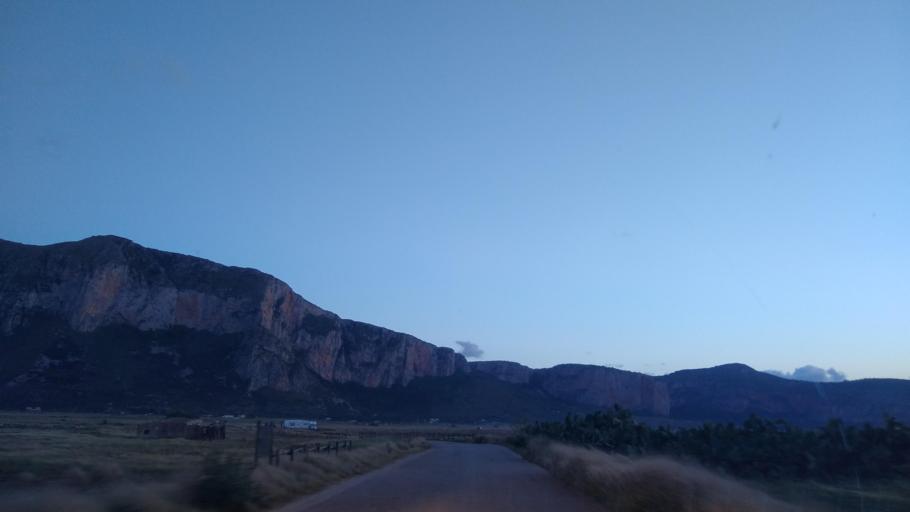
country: IT
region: Sicily
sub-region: Trapani
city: Castelluzzo
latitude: 38.1185
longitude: 12.7218
